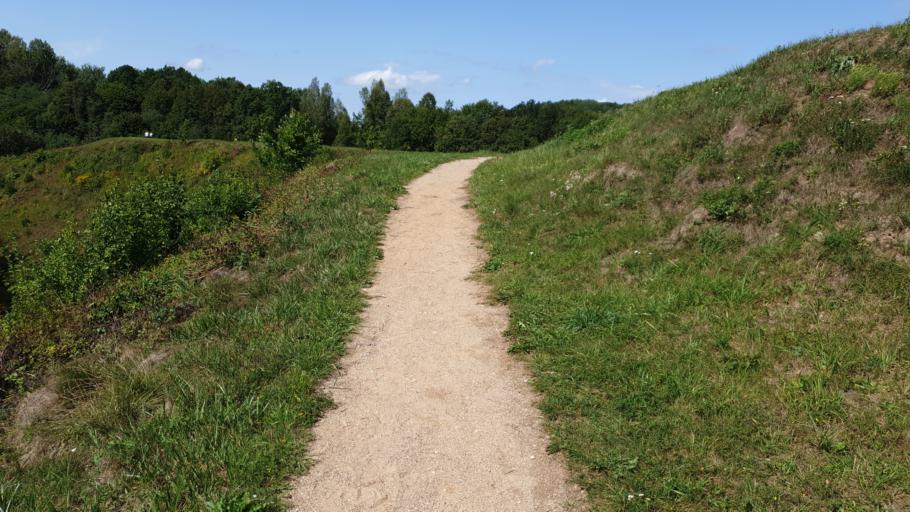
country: LT
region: Vilnius County
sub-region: Vilniaus Rajonas
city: Vievis
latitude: 54.8247
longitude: 24.9441
